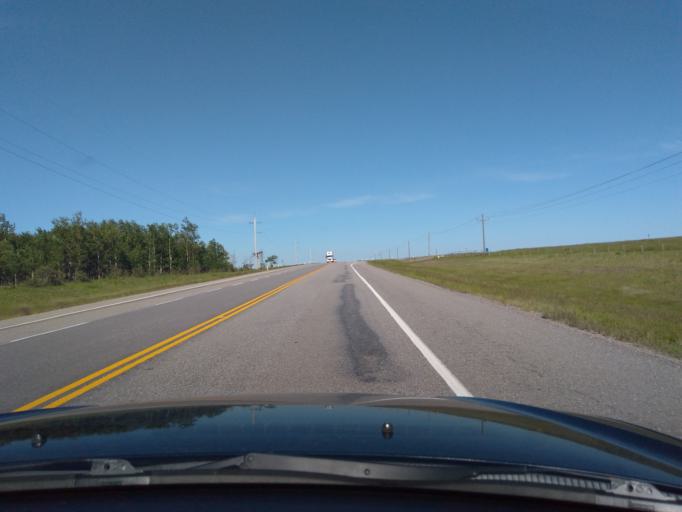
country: CA
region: Alberta
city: Cochrane
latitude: 51.0233
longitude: -114.4463
